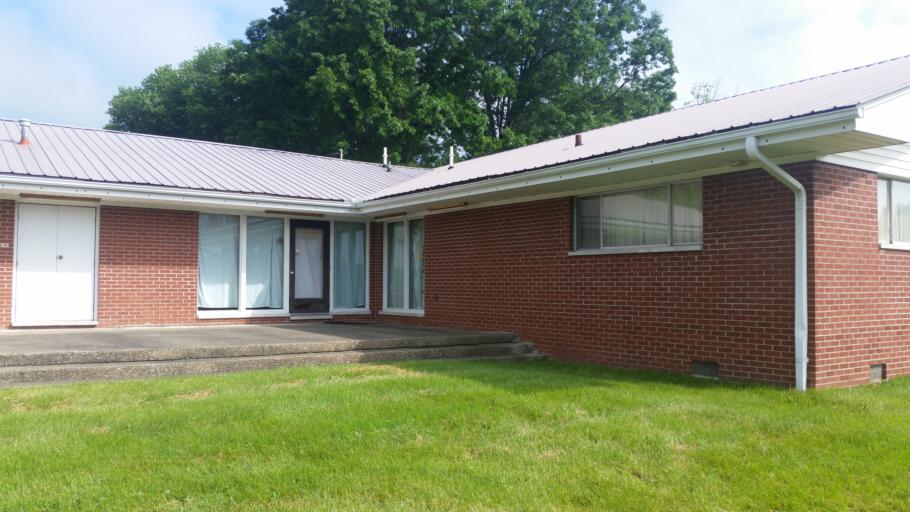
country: US
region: Kentucky
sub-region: Rowan County
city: Morehead
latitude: 38.1812
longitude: -83.4426
